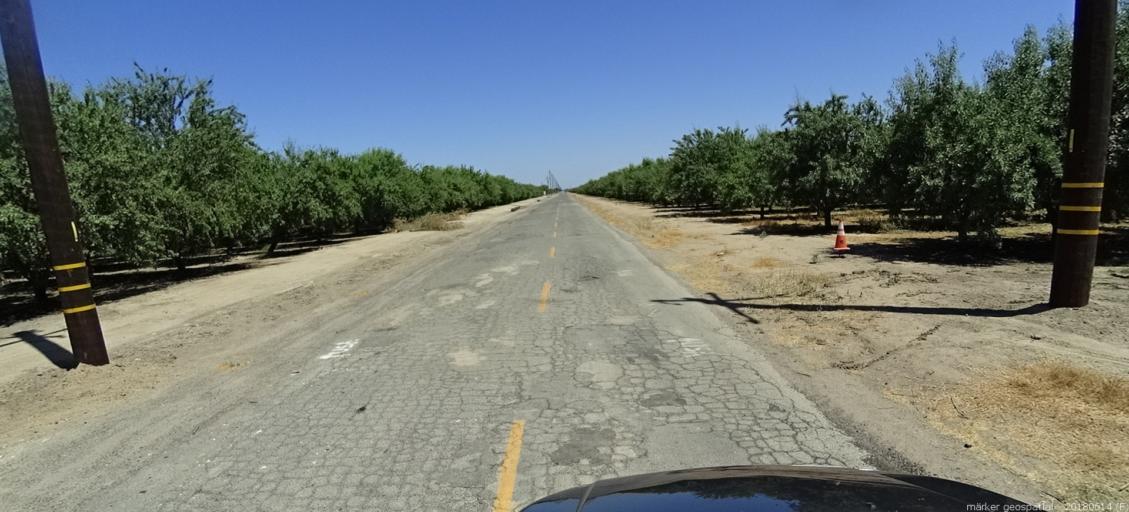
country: US
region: California
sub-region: Madera County
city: Fairmead
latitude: 37.0147
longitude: -120.2743
